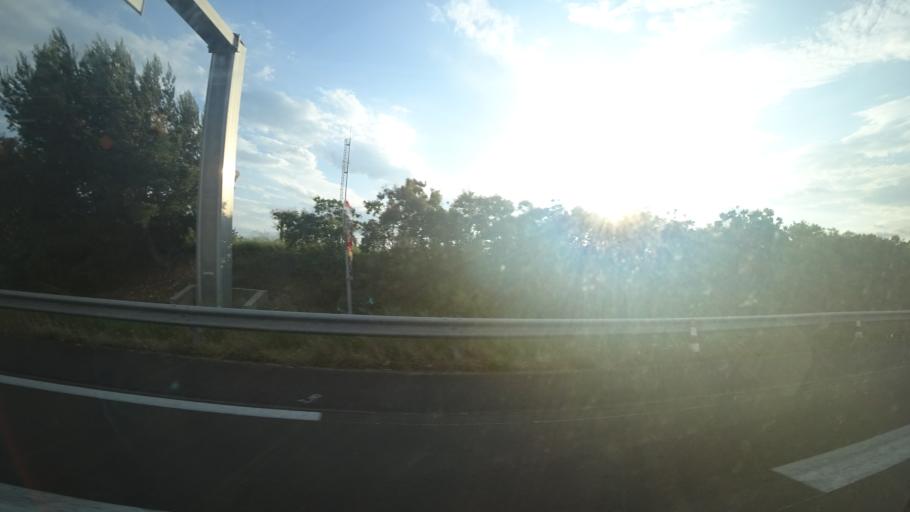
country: FR
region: Languedoc-Roussillon
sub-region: Departement de l'Herault
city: Nebian
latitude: 43.6167
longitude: 3.4593
